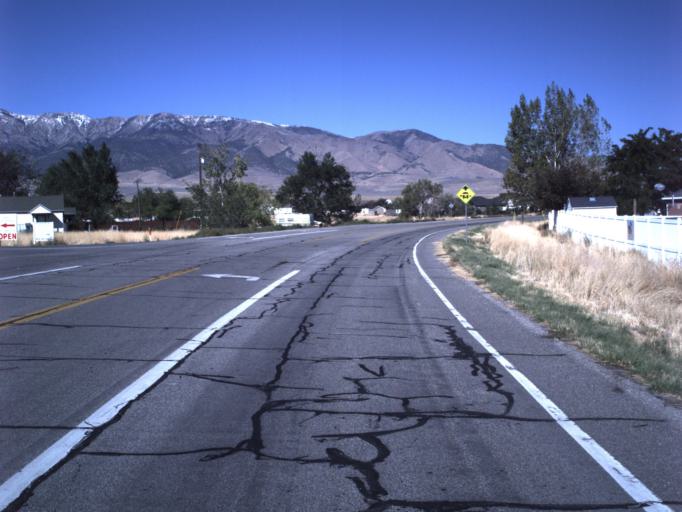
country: US
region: Utah
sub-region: Tooele County
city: Grantsville
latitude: 40.6003
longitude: -112.4816
